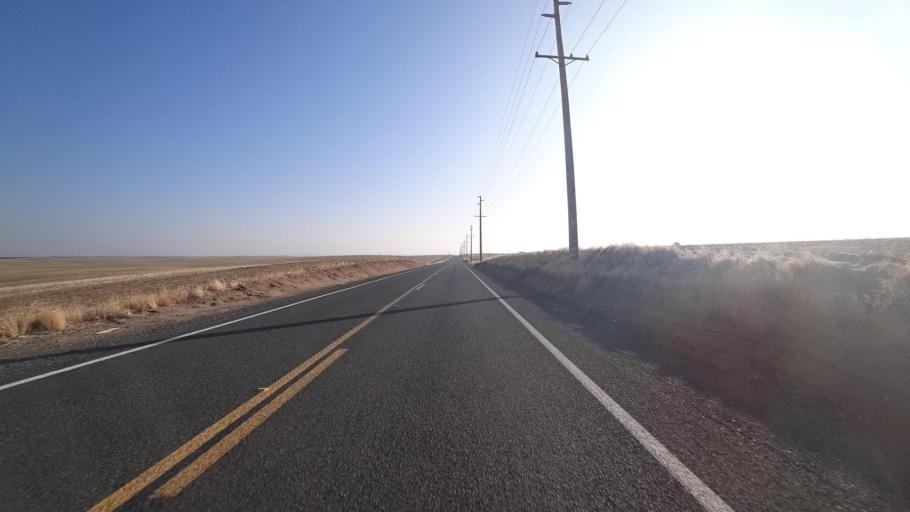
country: US
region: California
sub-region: Tulare County
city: Richgrove
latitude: 35.7619
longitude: -119.0772
